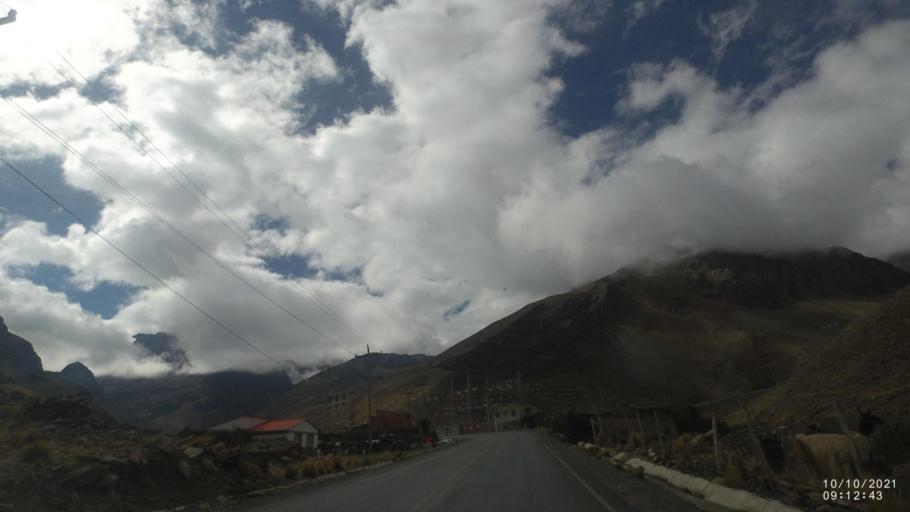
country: BO
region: La Paz
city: Quime
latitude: -17.0320
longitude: -67.2852
